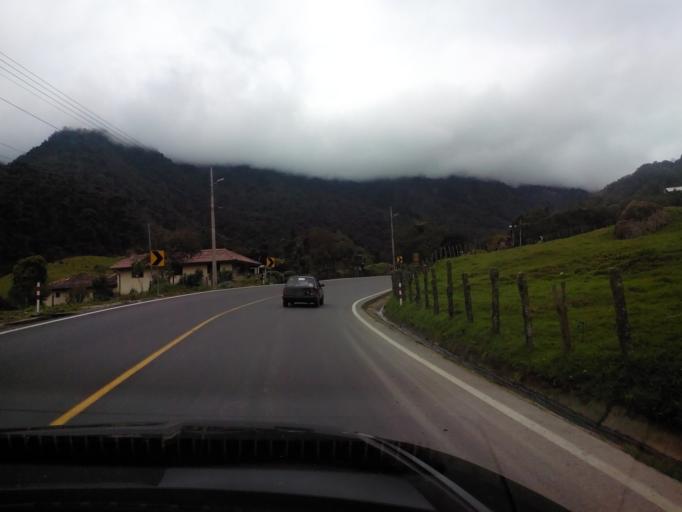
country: EC
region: Pichincha
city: Sangolqui
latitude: -0.3787
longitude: -78.1258
